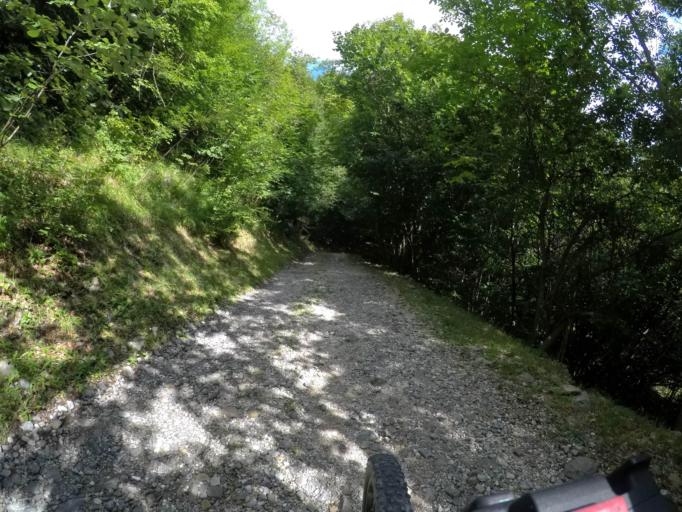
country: IT
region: Friuli Venezia Giulia
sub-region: Provincia di Udine
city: Moggio Udinese
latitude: 46.4876
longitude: 13.1884
